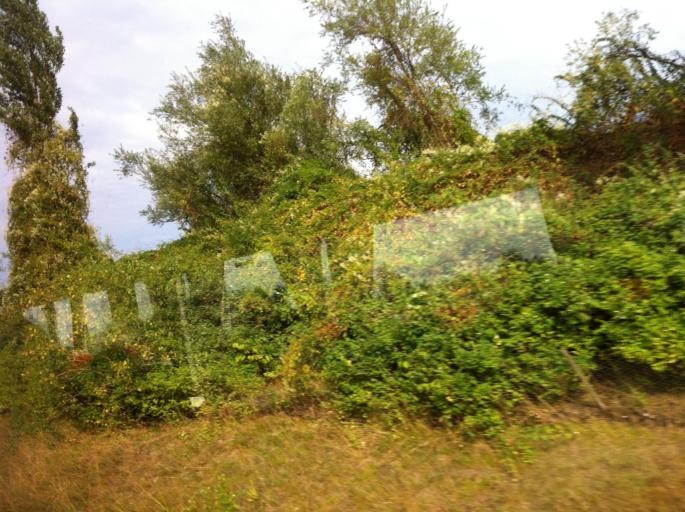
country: SE
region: Skane
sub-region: Kristianstads Kommun
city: Norra Asum
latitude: 55.9997
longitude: 14.1001
